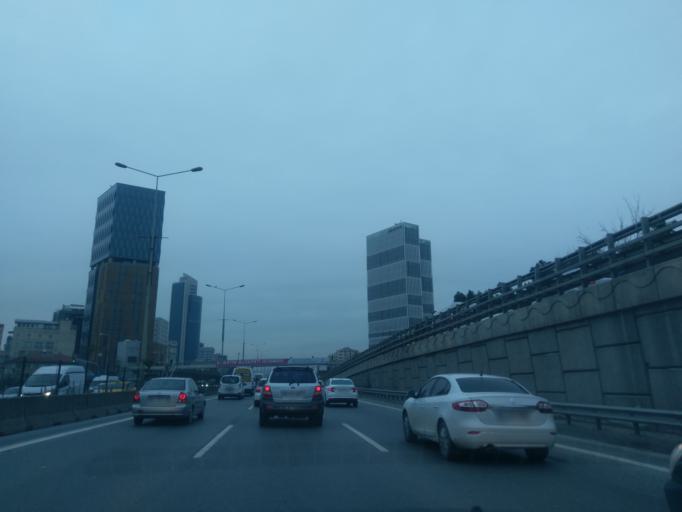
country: TR
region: Istanbul
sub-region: Atasehir
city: Atasehir
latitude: 40.9694
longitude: 29.1024
